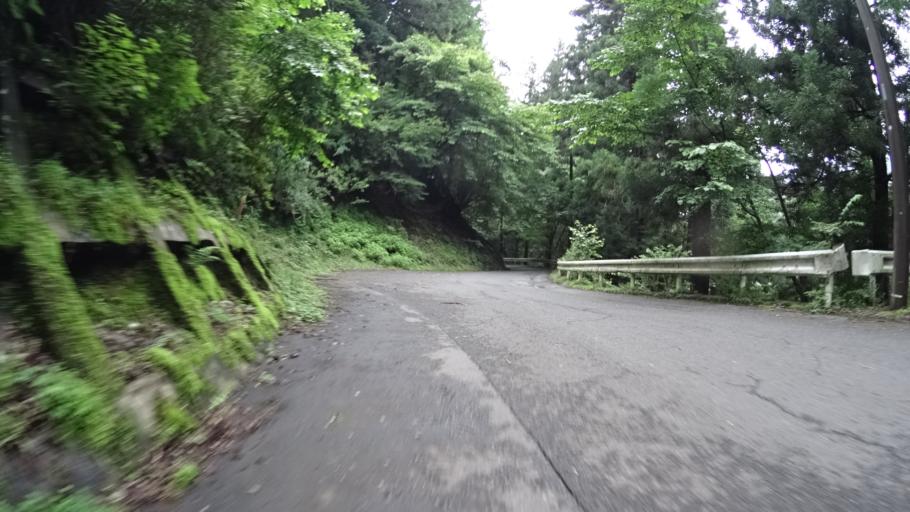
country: JP
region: Kanagawa
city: Hadano
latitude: 35.4724
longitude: 139.2111
